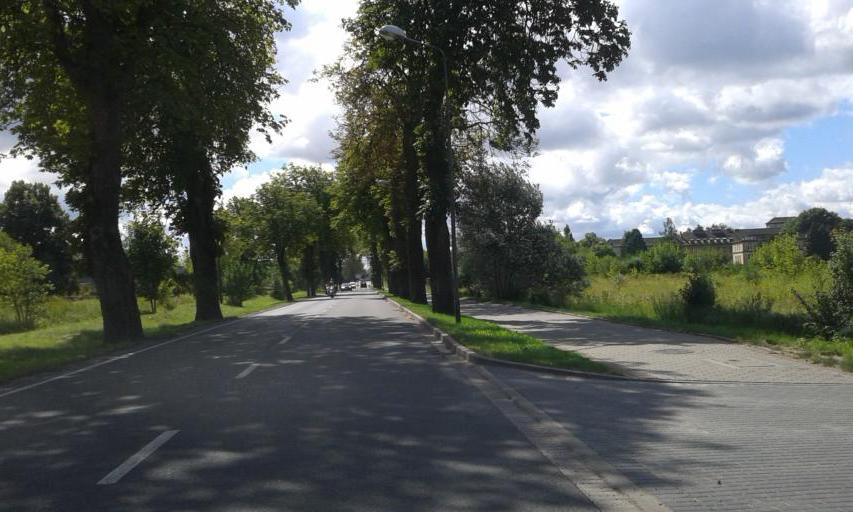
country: PL
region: West Pomeranian Voivodeship
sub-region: Powiat walecki
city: Walcz
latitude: 53.2856
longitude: 16.4609
